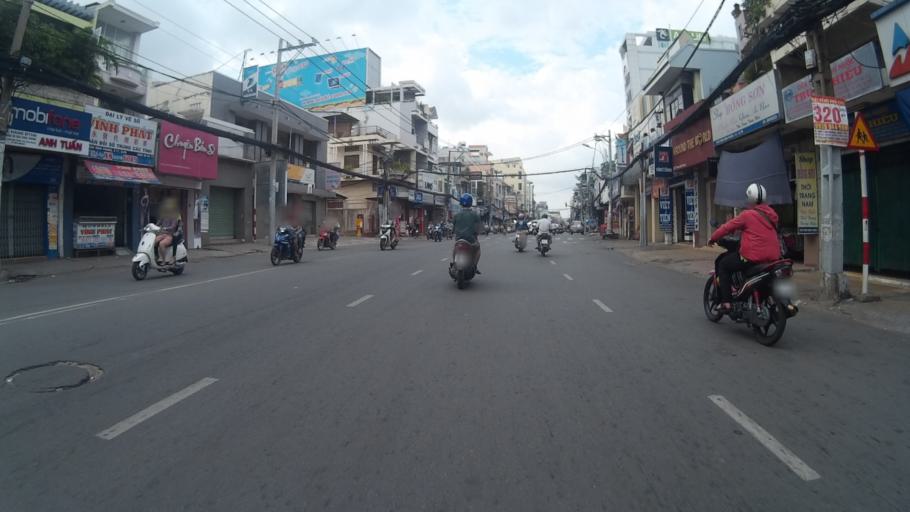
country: VN
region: Ho Chi Minh City
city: Quan Phu Nhuan
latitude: 10.7961
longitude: 106.6818
